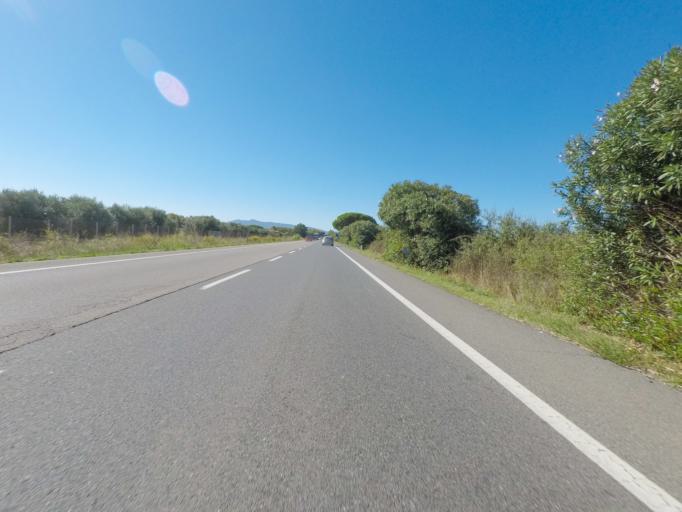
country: IT
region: Tuscany
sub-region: Provincia di Grosseto
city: Capalbio
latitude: 42.4152
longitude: 11.3613
